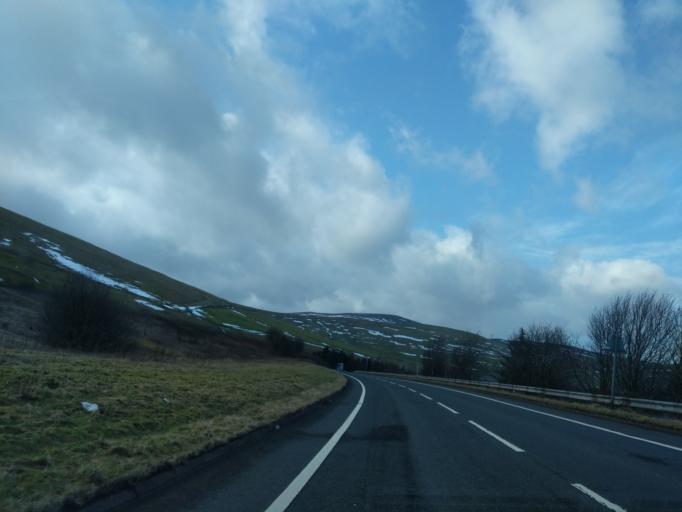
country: GB
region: Scotland
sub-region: South Lanarkshire
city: Douglas
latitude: 55.4683
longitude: -3.6619
